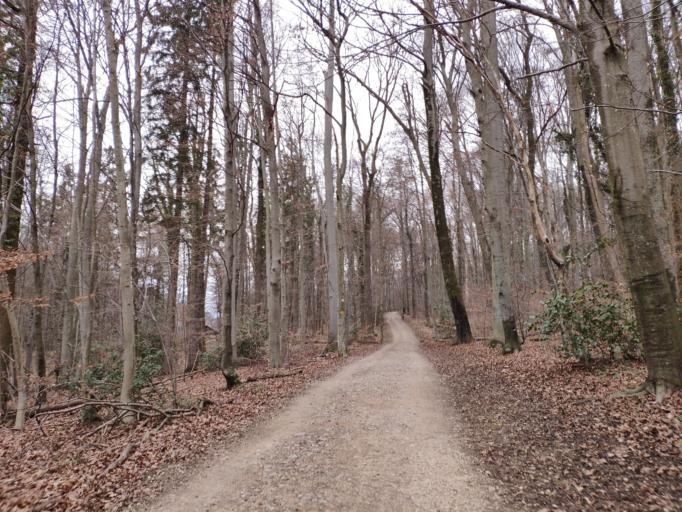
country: CH
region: Basel-City
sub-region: Basel-Stadt
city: Bettingen
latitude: 47.5632
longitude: 7.6571
